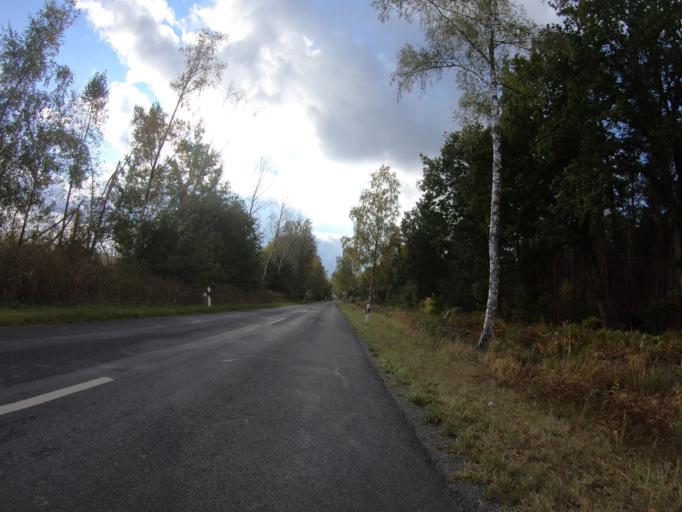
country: DE
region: Lower Saxony
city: Schoneworde
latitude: 52.5853
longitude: 10.6432
